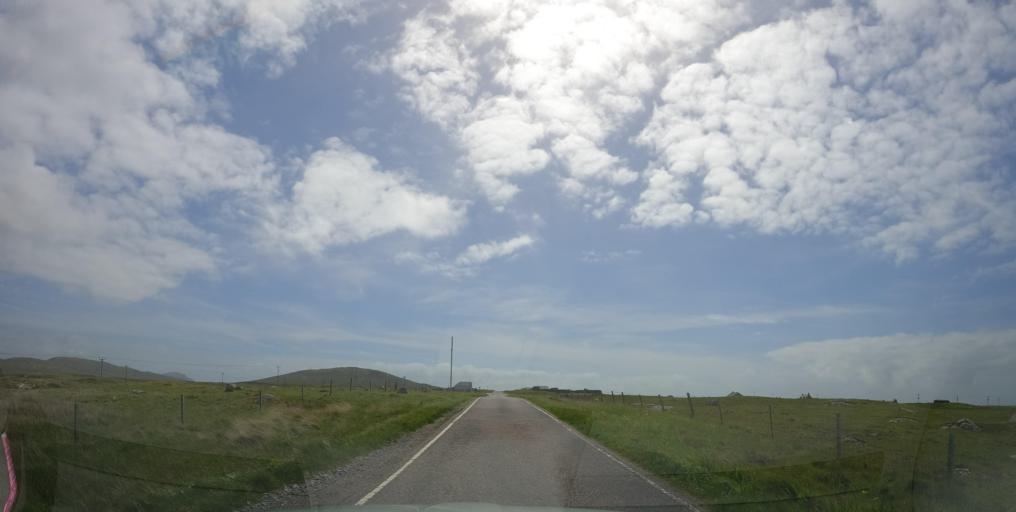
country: GB
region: Scotland
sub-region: Eilean Siar
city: Isle of South Uist
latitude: 57.2045
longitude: -7.3926
